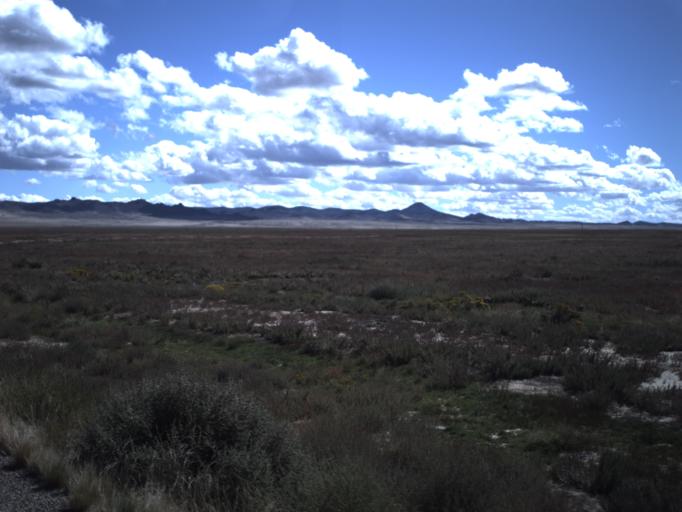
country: US
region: Utah
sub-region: Beaver County
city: Milford
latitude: 38.4689
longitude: -113.4023
